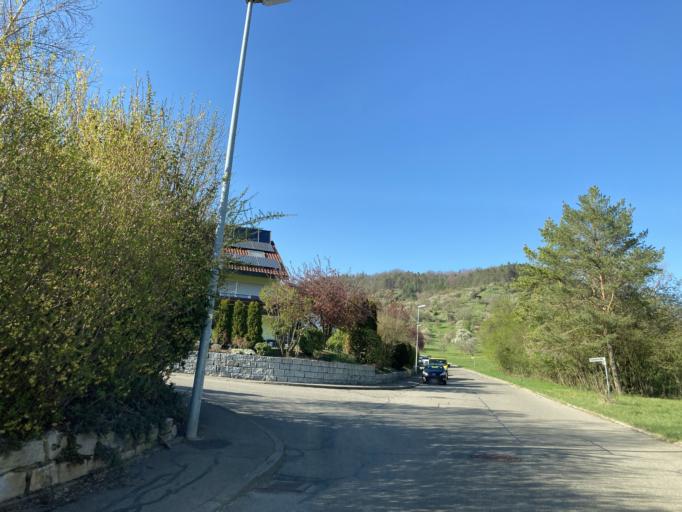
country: DE
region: Baden-Wuerttemberg
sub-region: Regierungsbezirk Stuttgart
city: Hildrizhausen
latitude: 48.5564
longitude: 8.9750
